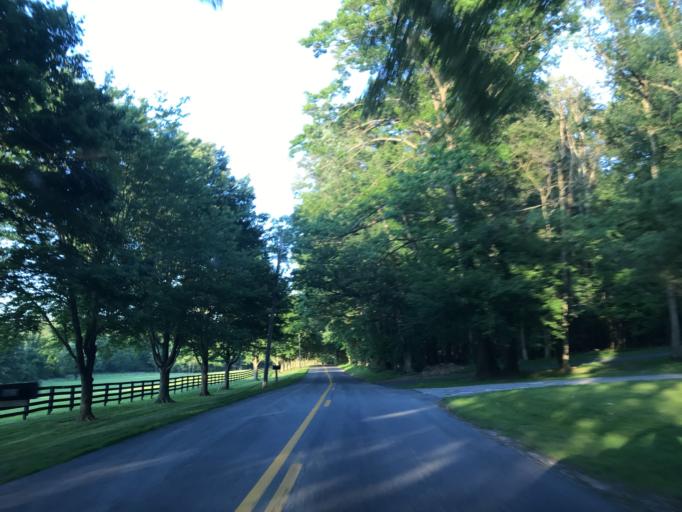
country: US
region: Maryland
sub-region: Baltimore County
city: Hunt Valley
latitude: 39.5631
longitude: -76.7012
